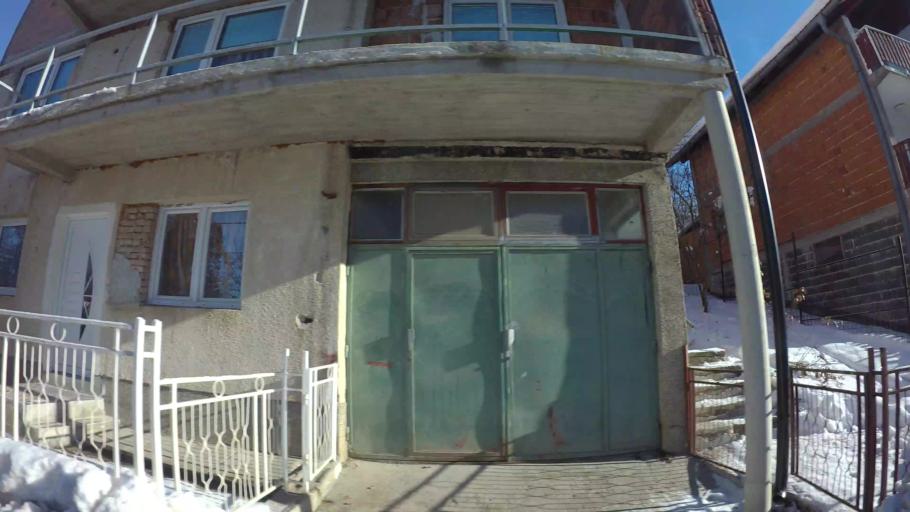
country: BA
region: Federation of Bosnia and Herzegovina
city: Kobilja Glava
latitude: 43.8893
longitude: 18.4094
